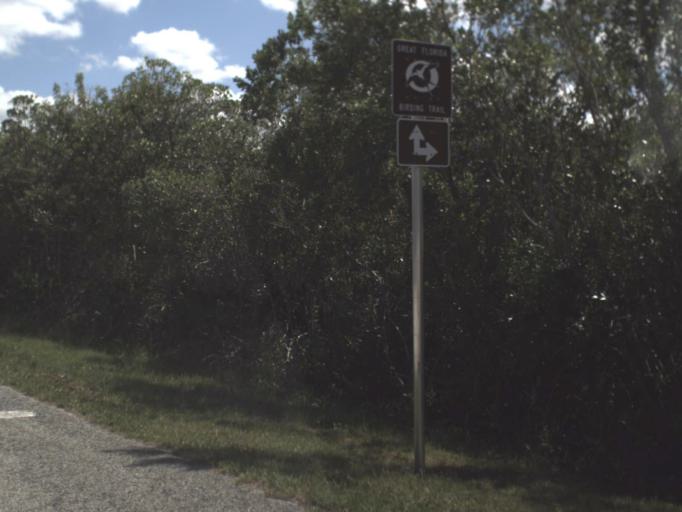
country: US
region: Florida
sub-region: Collier County
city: Marco
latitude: 25.9121
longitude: -81.3675
